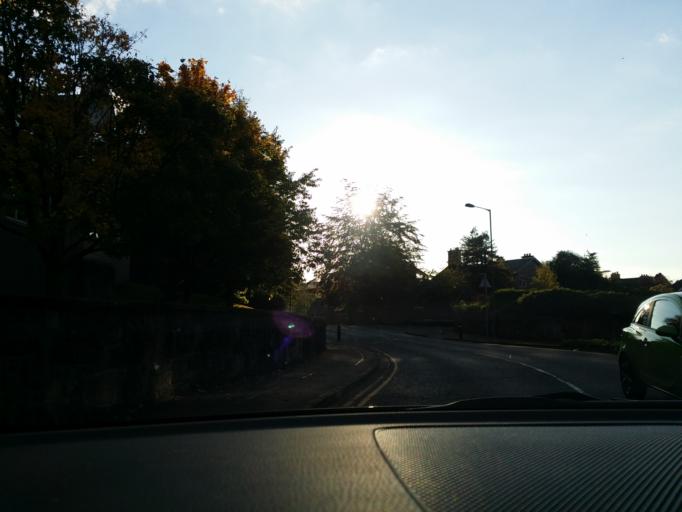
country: GB
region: Scotland
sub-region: Stirling
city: Stirling
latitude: 56.1110
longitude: -3.9495
